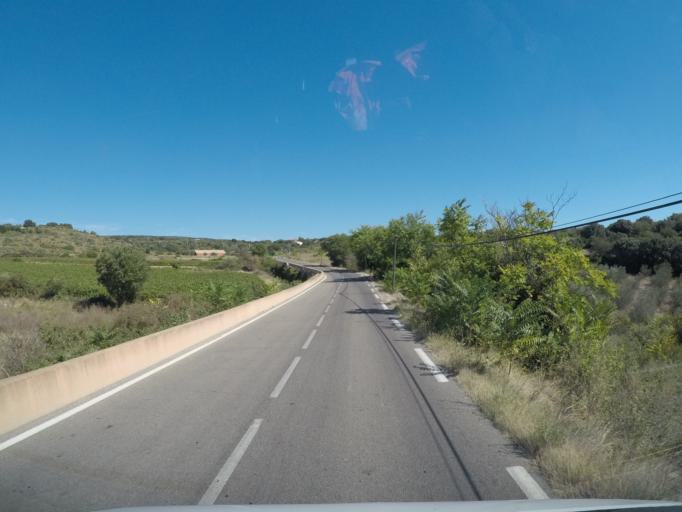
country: FR
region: Languedoc-Roussillon
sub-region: Departement de l'Herault
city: Aniane
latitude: 43.7114
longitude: 3.6077
